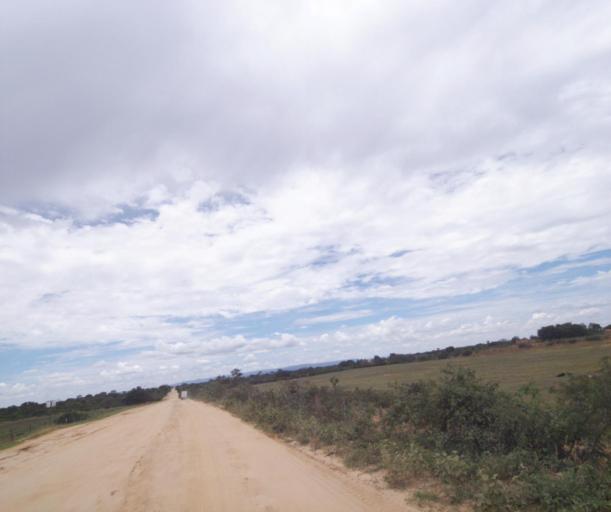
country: BR
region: Bahia
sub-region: Carinhanha
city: Carinhanha
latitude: -14.2796
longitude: -43.7949
